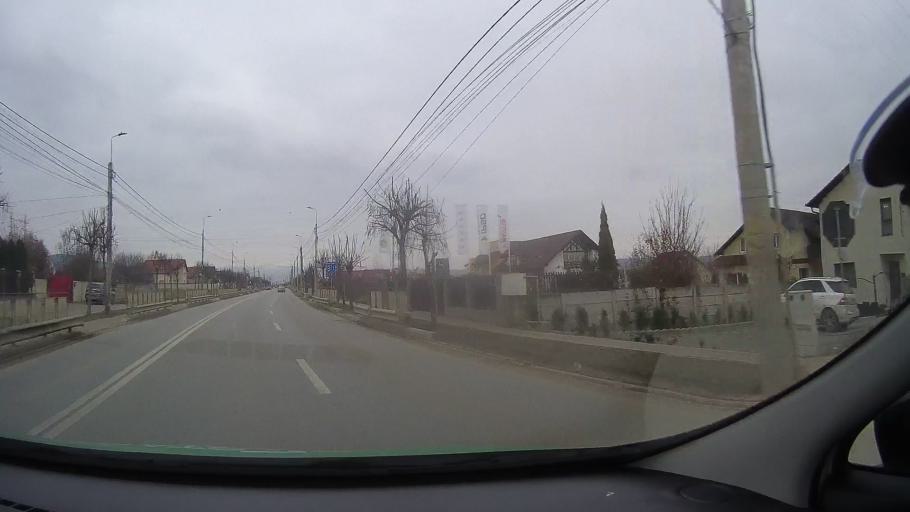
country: RO
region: Alba
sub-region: Municipiul Alba Iulia
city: Micesti
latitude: 46.0892
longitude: 23.5566
